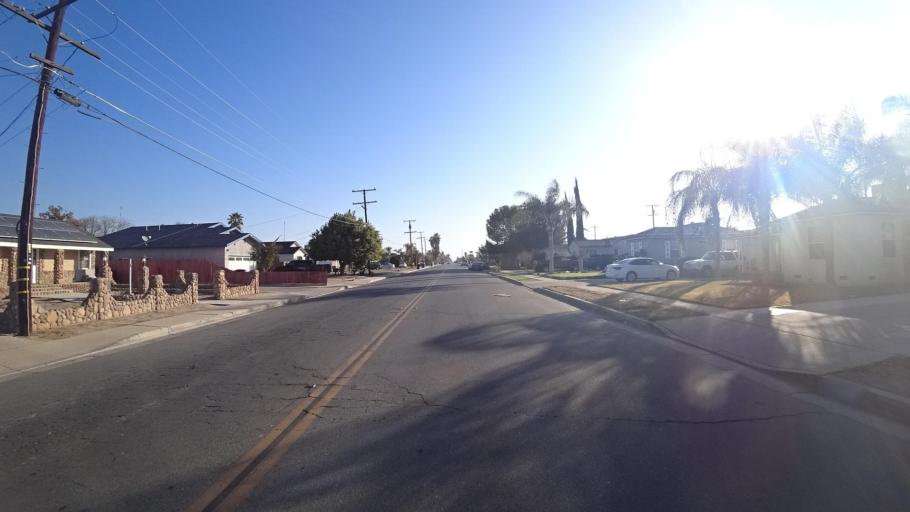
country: US
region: California
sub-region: Kern County
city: Delano
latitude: 35.7687
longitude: -119.2398
